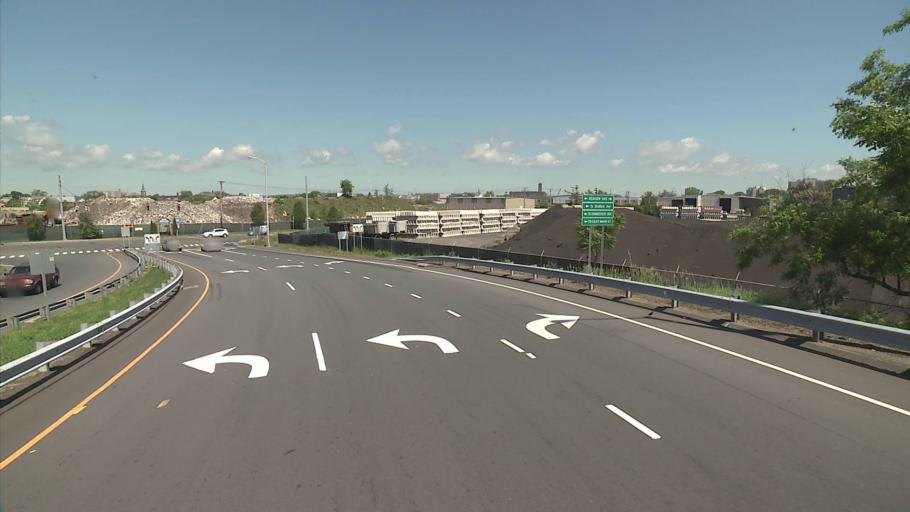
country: US
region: Connecticut
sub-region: Fairfield County
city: Bridgeport
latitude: 41.1786
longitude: -73.1720
